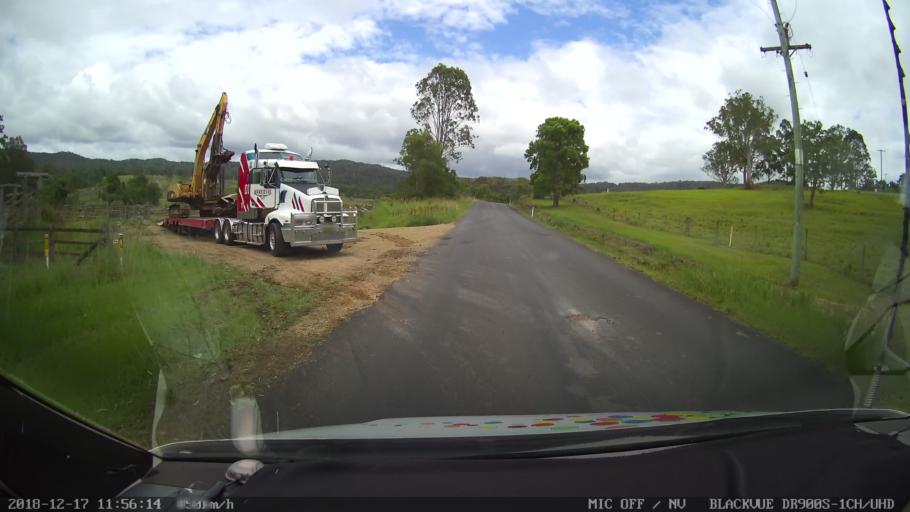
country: AU
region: New South Wales
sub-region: Kyogle
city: Kyogle
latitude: -28.5492
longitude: 152.5814
